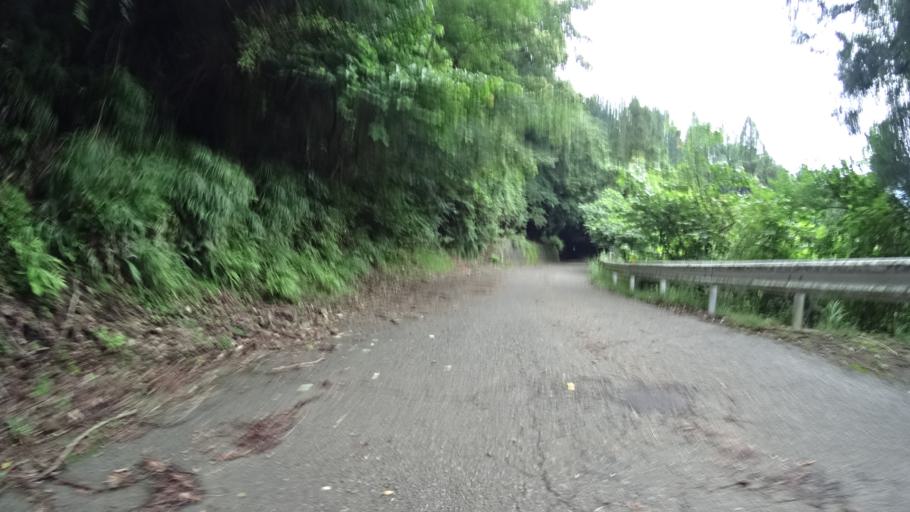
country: JP
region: Kanagawa
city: Atsugi
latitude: 35.5017
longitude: 139.2747
